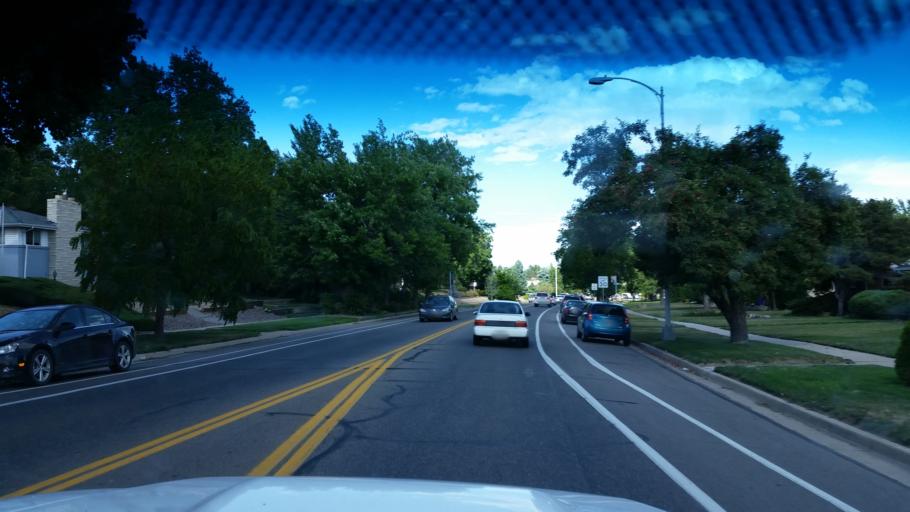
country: US
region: Colorado
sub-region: Broomfield County
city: Broomfield
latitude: 39.9246
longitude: -105.0758
